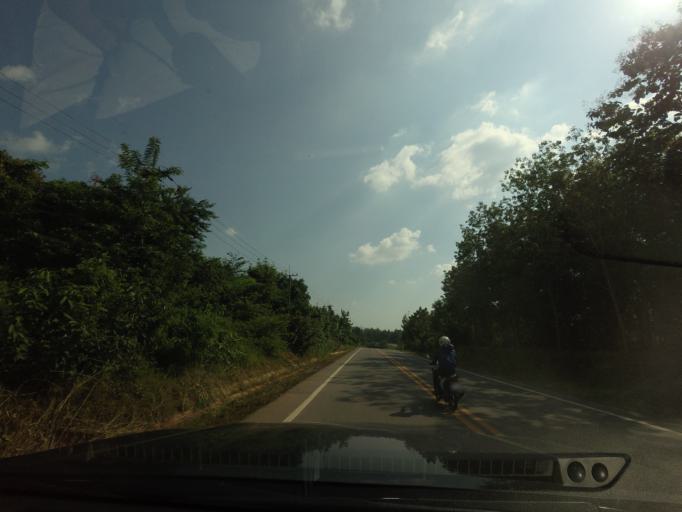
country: TH
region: Nan
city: Santi Suk
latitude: 18.9634
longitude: 100.9241
